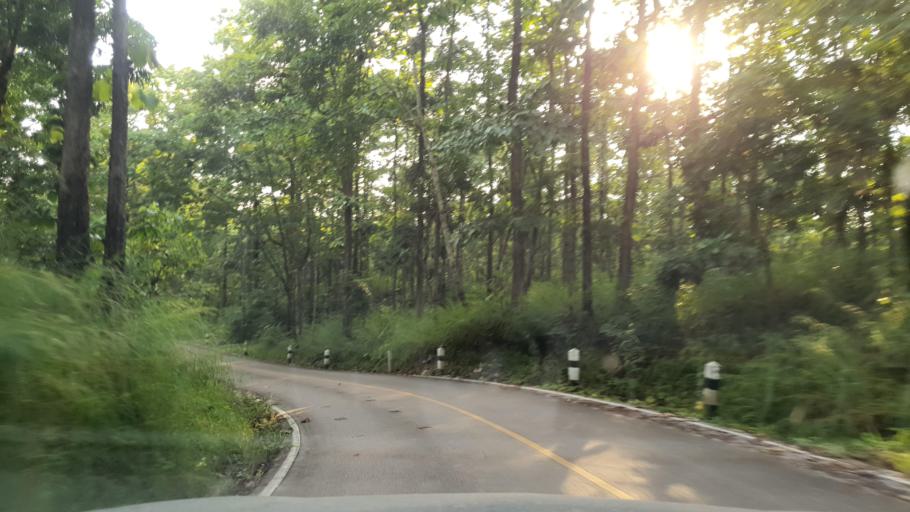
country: TH
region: Chiang Mai
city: Mae On
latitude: 18.8723
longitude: 99.2470
